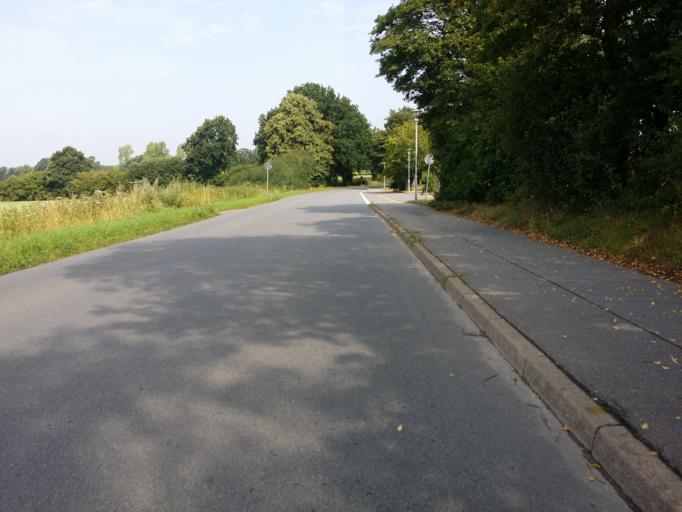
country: DE
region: Schleswig-Holstein
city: Heiligenstedten
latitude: 53.9422
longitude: 9.4684
